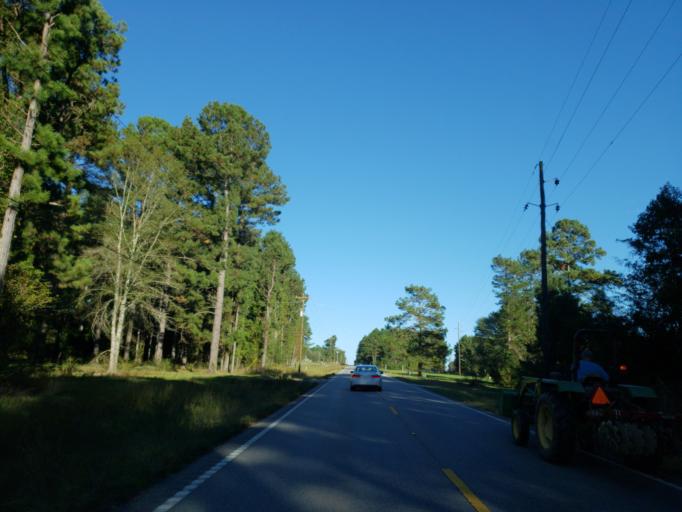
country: US
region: Mississippi
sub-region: Perry County
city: Richton
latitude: 31.3579
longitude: -89.0163
